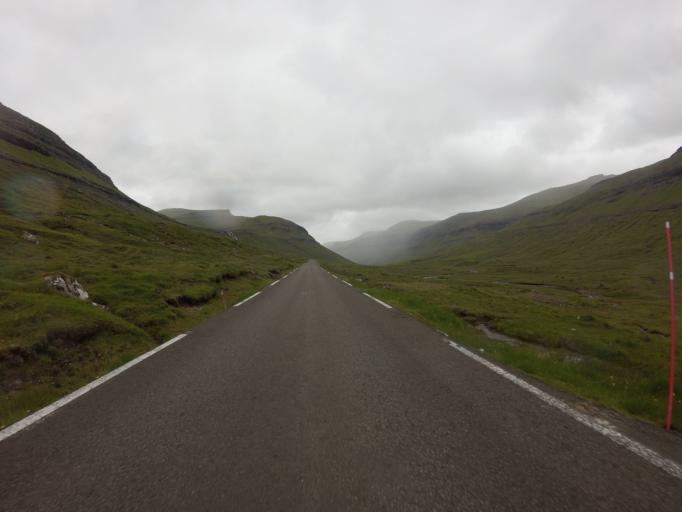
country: FO
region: Streymoy
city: Vestmanna
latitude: 62.2167
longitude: -7.1197
